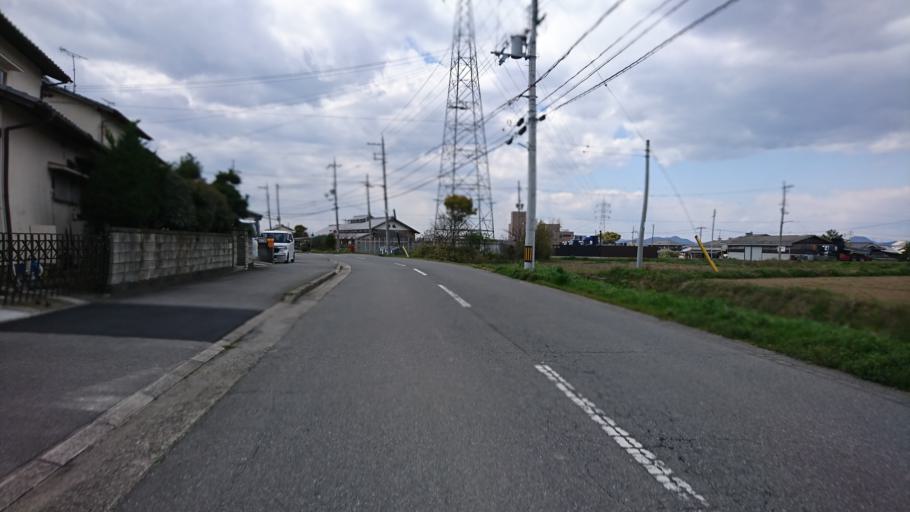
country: JP
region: Hyogo
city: Miki
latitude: 34.7539
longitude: 134.9153
